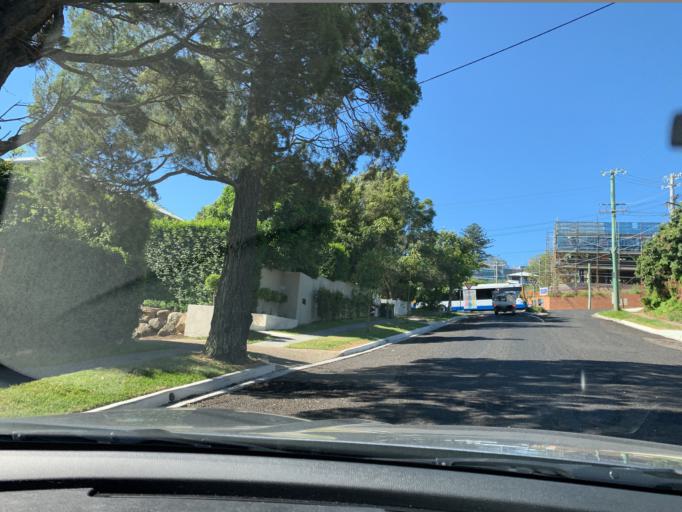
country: AU
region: Queensland
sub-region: Brisbane
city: Ascot
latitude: -27.4335
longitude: 153.0490
